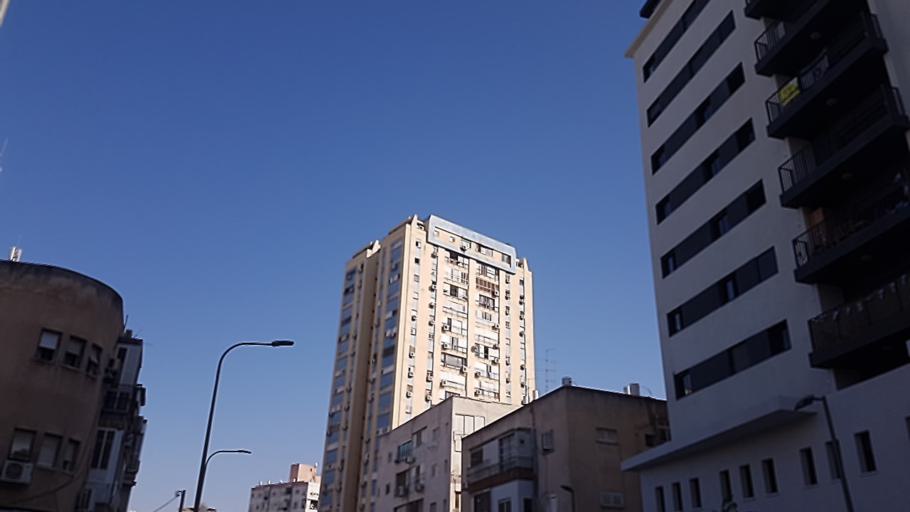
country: IL
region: Tel Aviv
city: Ramat Gan
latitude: 32.0794
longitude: 34.8136
